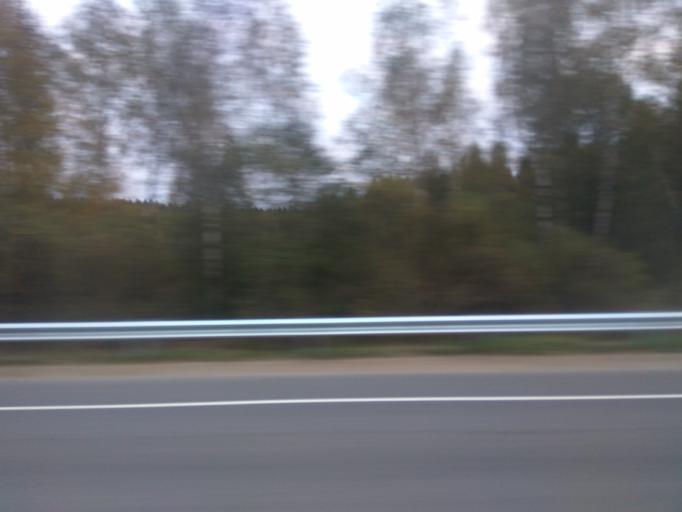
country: RU
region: Moskovskaya
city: Krasnoarmeysk
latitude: 56.0275
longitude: 38.1814
